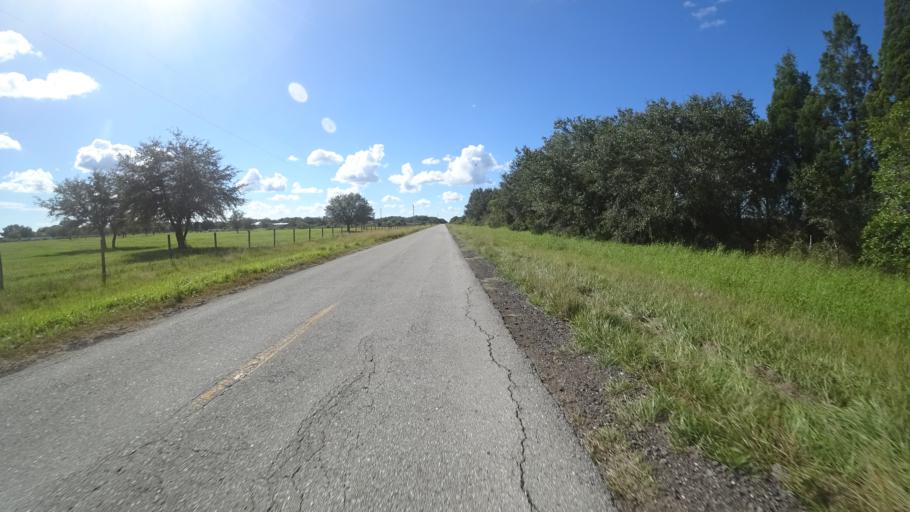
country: US
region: Florida
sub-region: Sarasota County
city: Warm Mineral Springs
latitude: 27.2736
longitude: -82.1477
